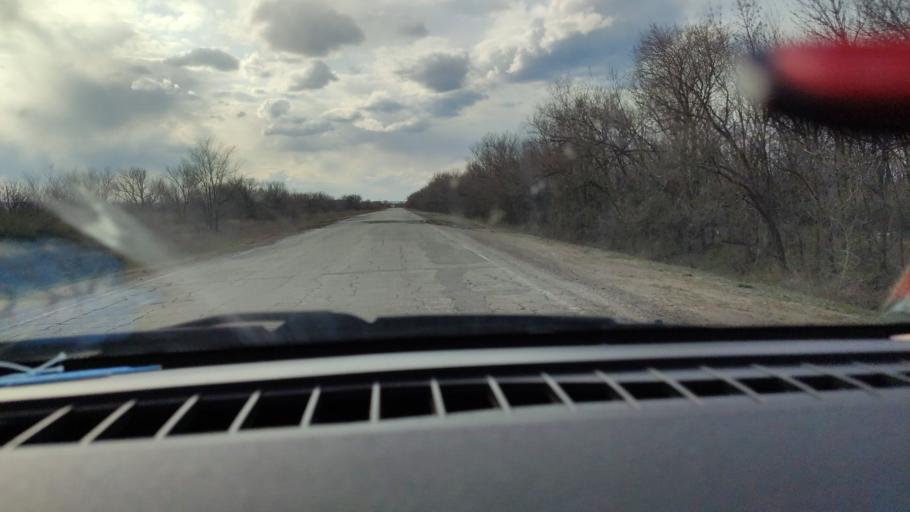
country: RU
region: Saratov
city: Krasnoarmeysk
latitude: 51.0700
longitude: 45.9915
